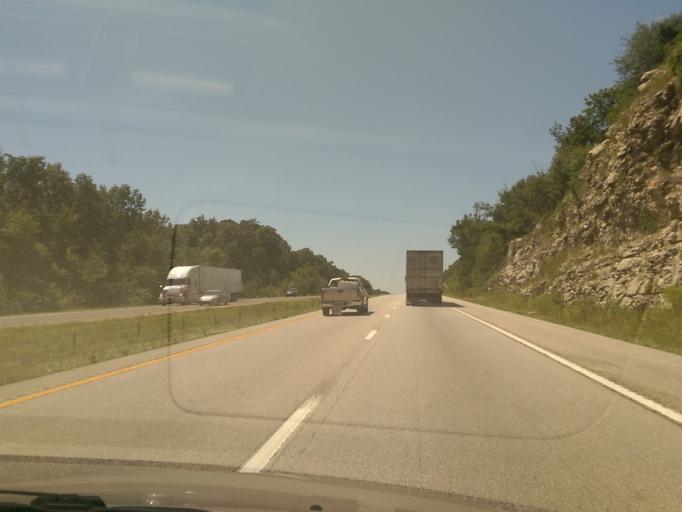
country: US
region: Missouri
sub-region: Cooper County
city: Boonville
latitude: 38.9339
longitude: -92.9497
